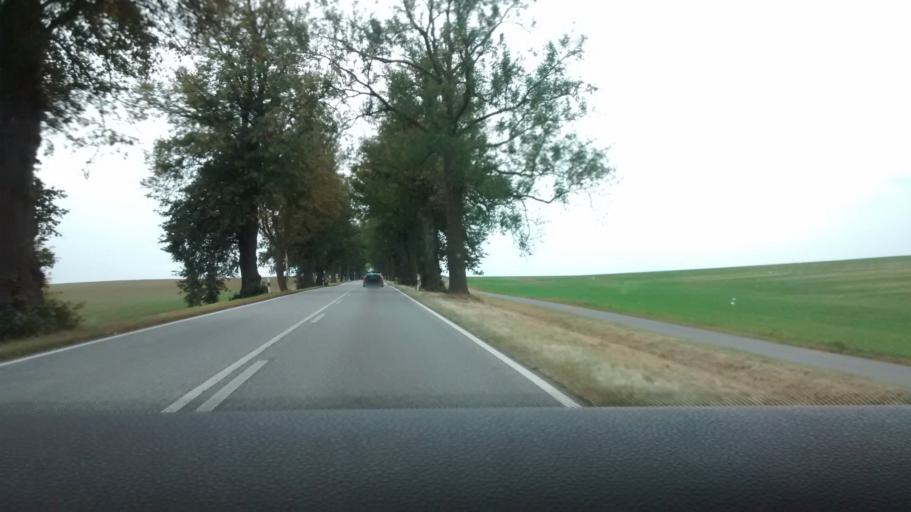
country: DE
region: Mecklenburg-Vorpommern
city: Mecklenburg
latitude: 53.8364
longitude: 11.4572
